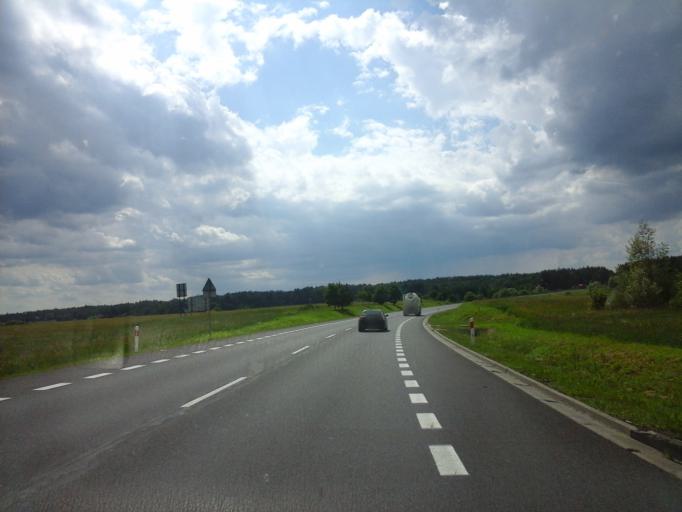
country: PL
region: West Pomeranian Voivodeship
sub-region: Powiat bialogardzki
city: Karlino
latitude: 54.0287
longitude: 15.8877
